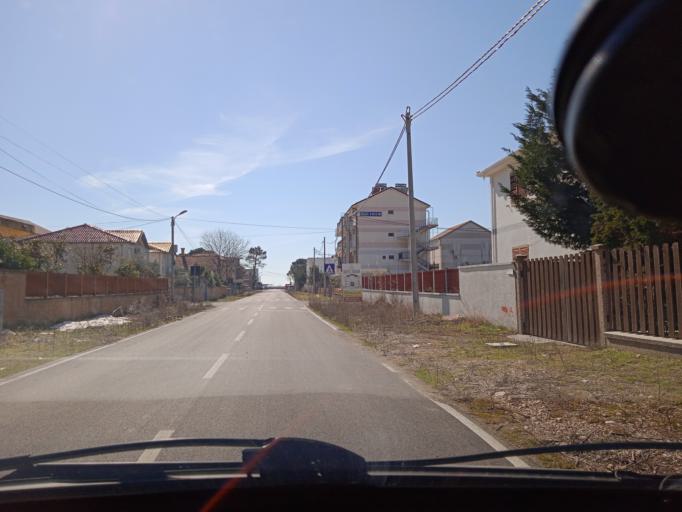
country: AL
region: Shkoder
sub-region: Rrethi i Shkodres
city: Velipoje
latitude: 41.8657
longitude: 19.4105
